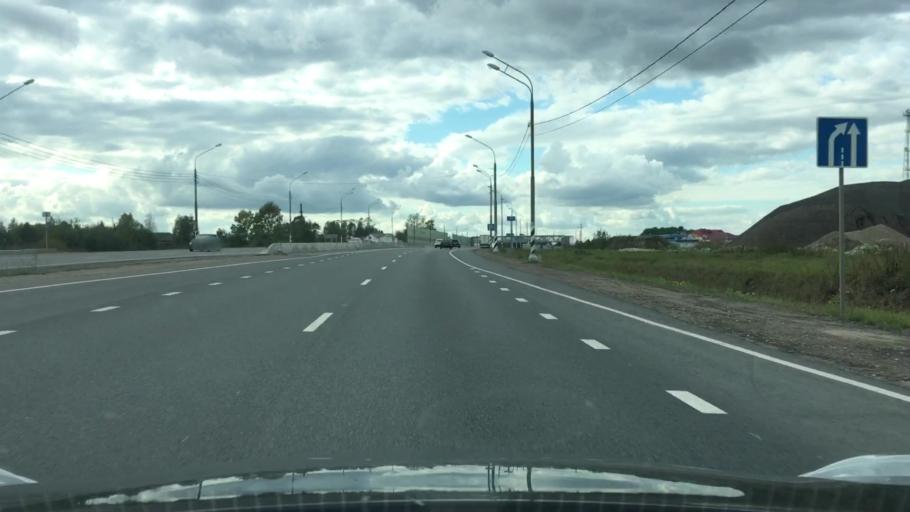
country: RU
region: Tverskaya
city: Tver
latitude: 56.7825
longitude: 35.9518
